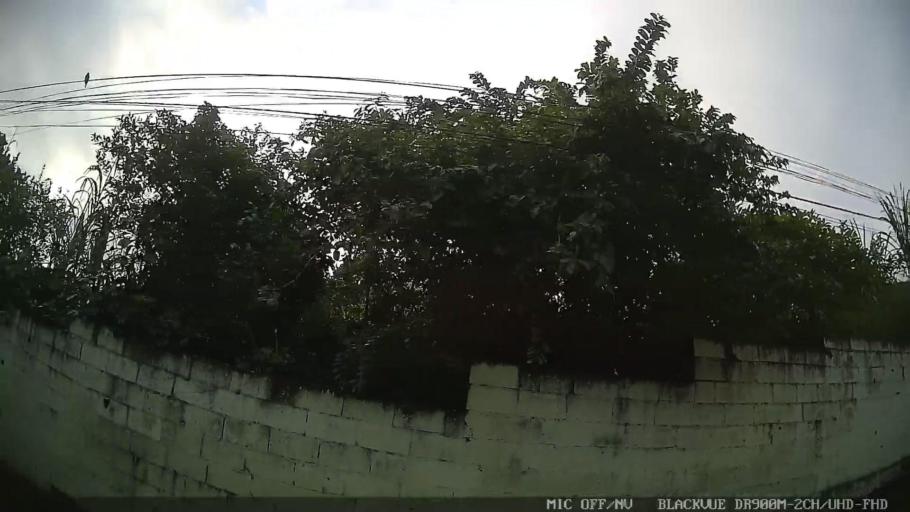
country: BR
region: Sao Paulo
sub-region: Guaruja
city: Guaruja
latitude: -23.9909
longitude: -46.1952
